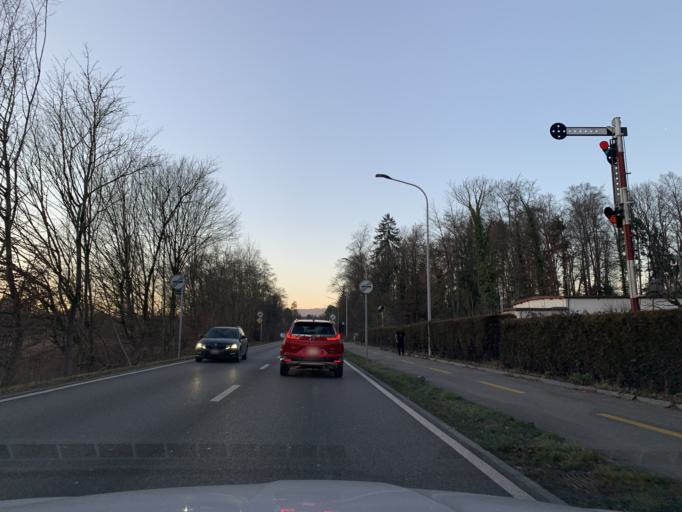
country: CH
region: Zurich
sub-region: Bezirk Zuerich
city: Zuerich (Kreis 10) / Ruetihof
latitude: 47.4288
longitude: 8.4888
